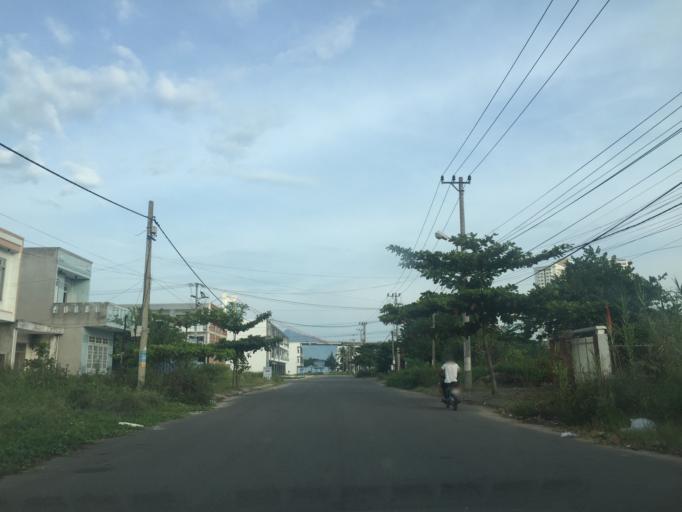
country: VN
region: Da Nang
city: Da Nang
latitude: 16.0929
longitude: 108.2270
